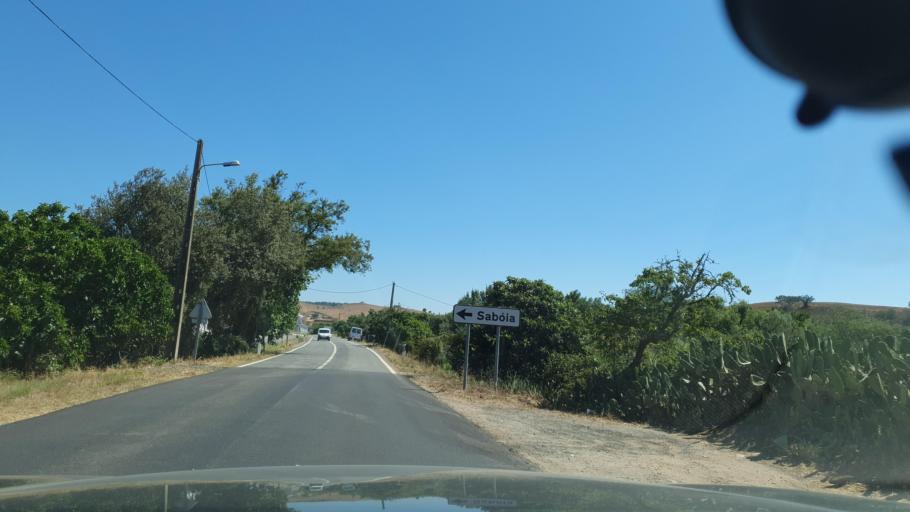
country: PT
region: Faro
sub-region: Monchique
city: Monchique
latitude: 37.4844
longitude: -8.4880
